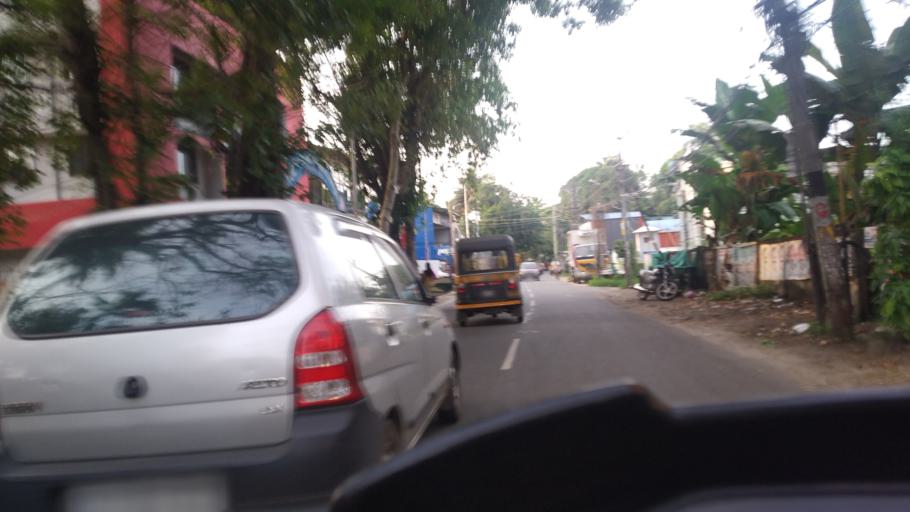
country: IN
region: Kerala
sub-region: Ernakulam
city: Elur
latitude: 10.0134
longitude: 76.2860
